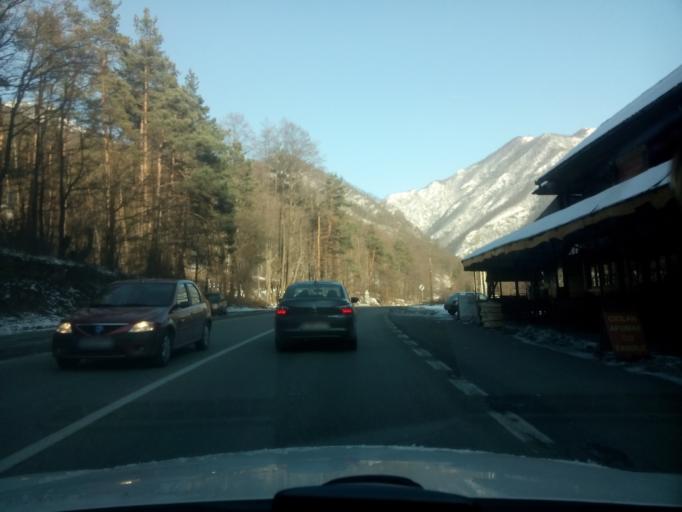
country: RO
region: Valcea
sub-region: Comuna Brezoi
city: Brezoi
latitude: 45.3107
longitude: 24.2689
